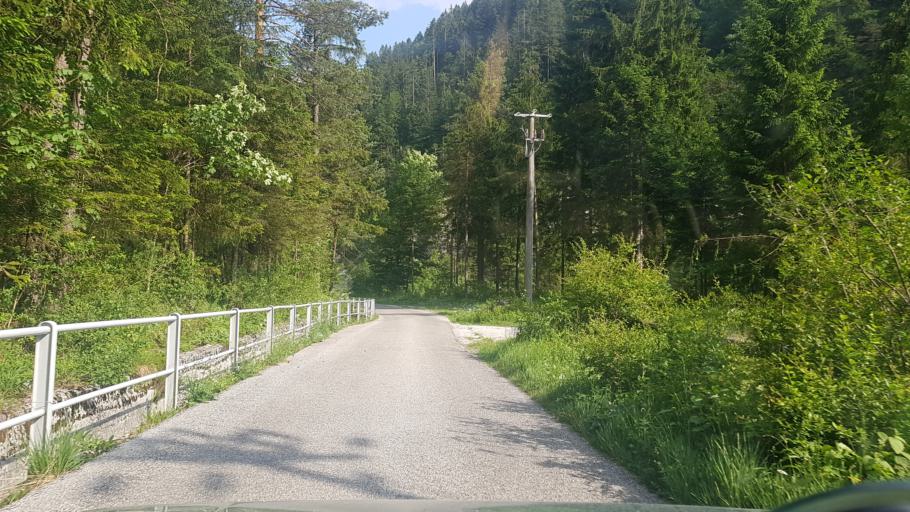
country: IT
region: Friuli Venezia Giulia
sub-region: Provincia di Udine
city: Pontebba
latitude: 46.5261
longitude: 13.2517
